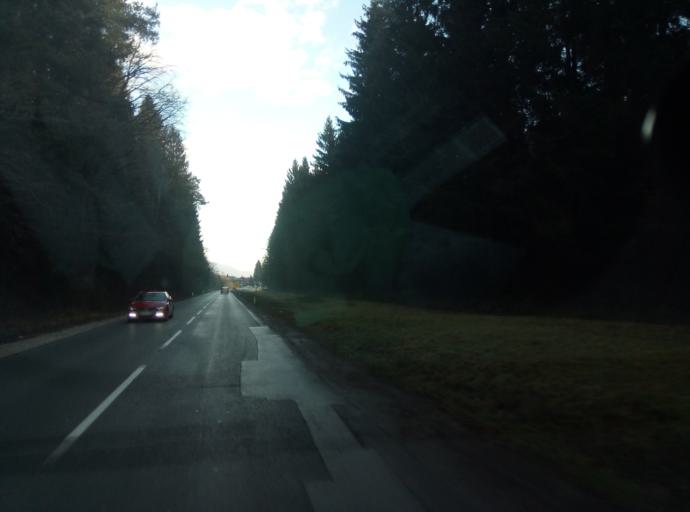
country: SI
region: Kranj
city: Mlaka pri Kranju
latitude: 46.2685
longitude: 14.3436
